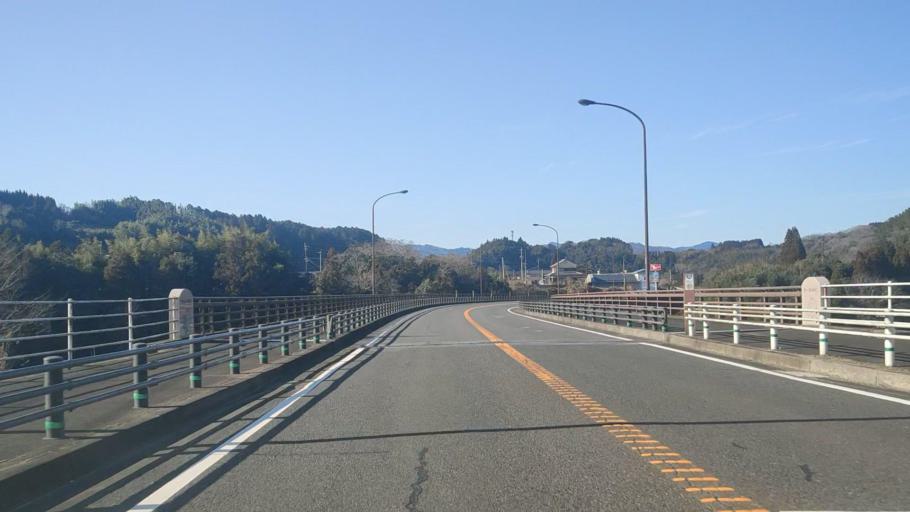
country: JP
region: Oita
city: Usuki
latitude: 33.0575
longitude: 131.6751
